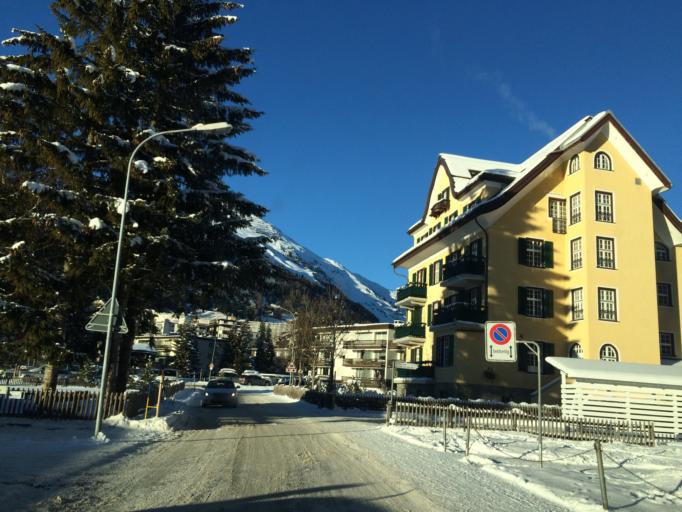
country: CH
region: Grisons
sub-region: Praettigau/Davos District
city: Davos
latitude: 46.7985
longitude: 9.8349
